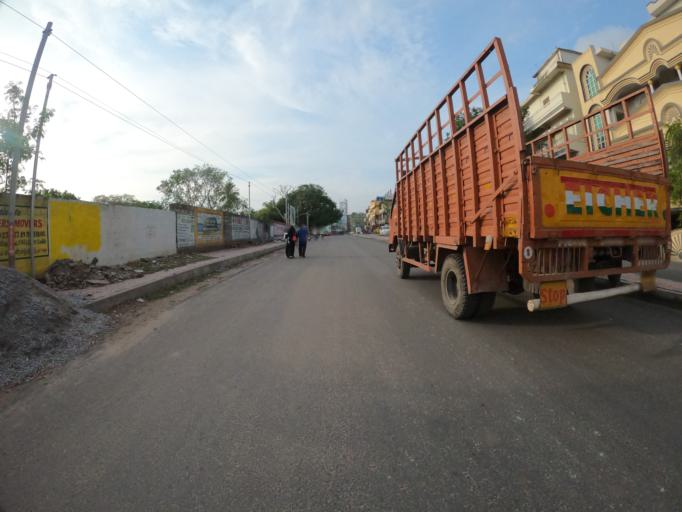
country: IN
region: Telangana
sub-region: Hyderabad
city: Hyderabad
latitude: 17.4112
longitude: 78.3949
